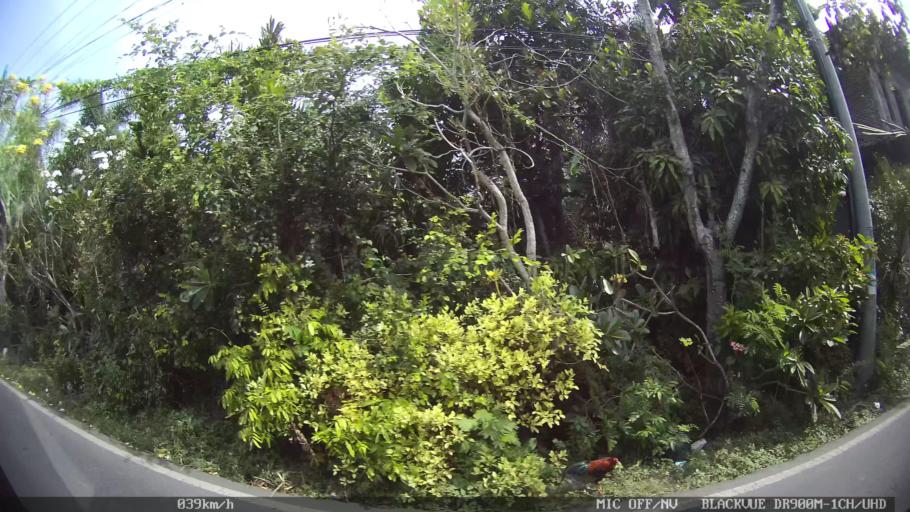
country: ID
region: Daerah Istimewa Yogyakarta
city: Depok
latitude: -7.8046
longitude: 110.4253
